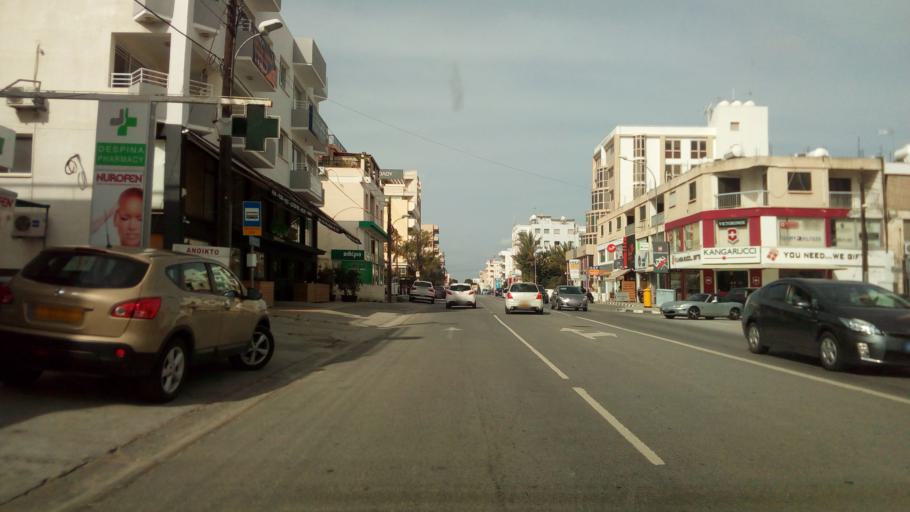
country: CY
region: Lefkosia
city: Nicosia
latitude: 35.1430
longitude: 33.3667
